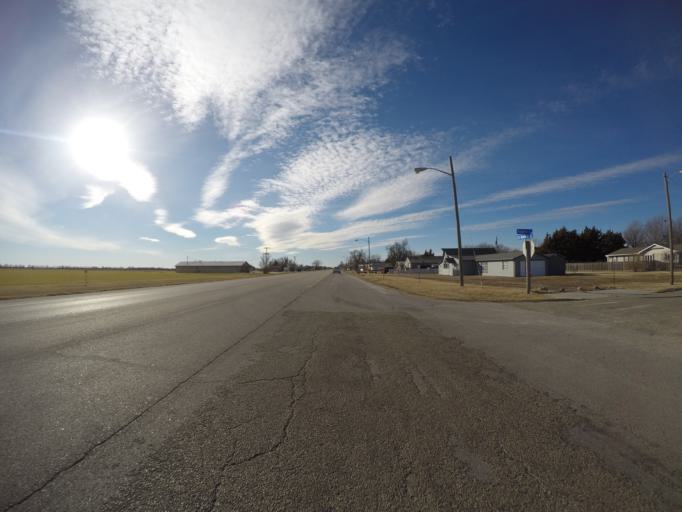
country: US
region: Kansas
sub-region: McPherson County
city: McPherson
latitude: 38.3771
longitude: -97.5348
